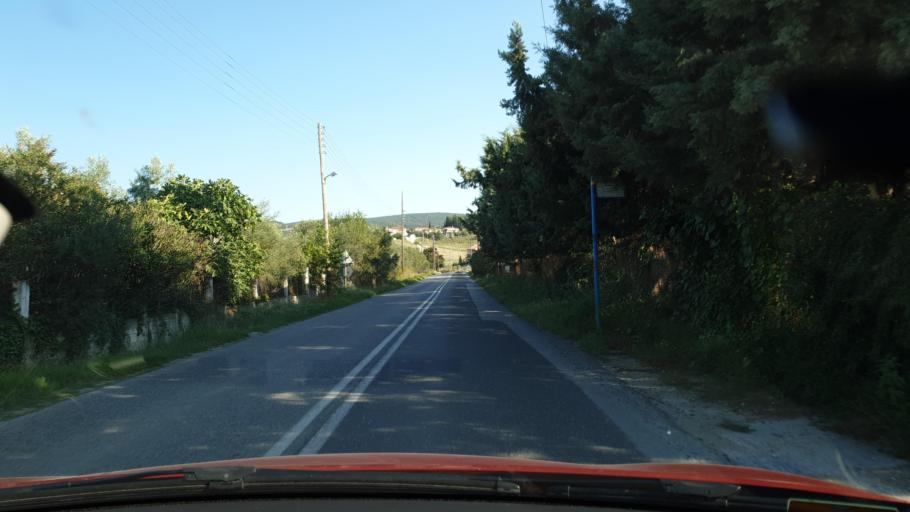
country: GR
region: Central Macedonia
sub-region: Nomos Thessalonikis
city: Agia Paraskevi
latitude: 40.4867
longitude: 23.0414
